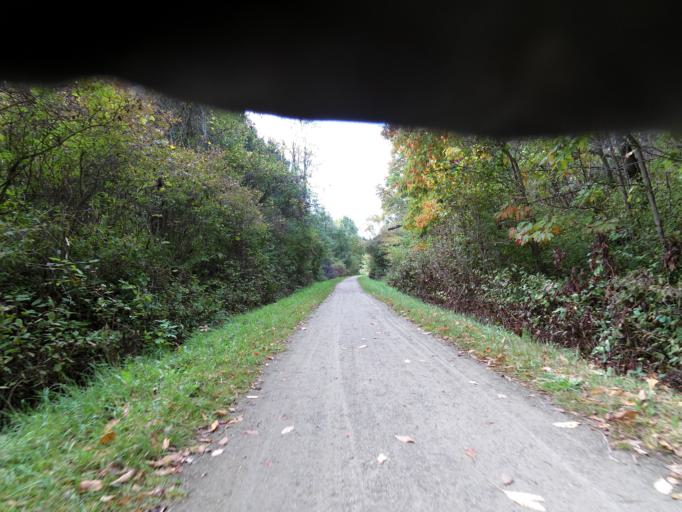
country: CA
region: Ontario
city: Ancaster
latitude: 43.2346
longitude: -80.0432
